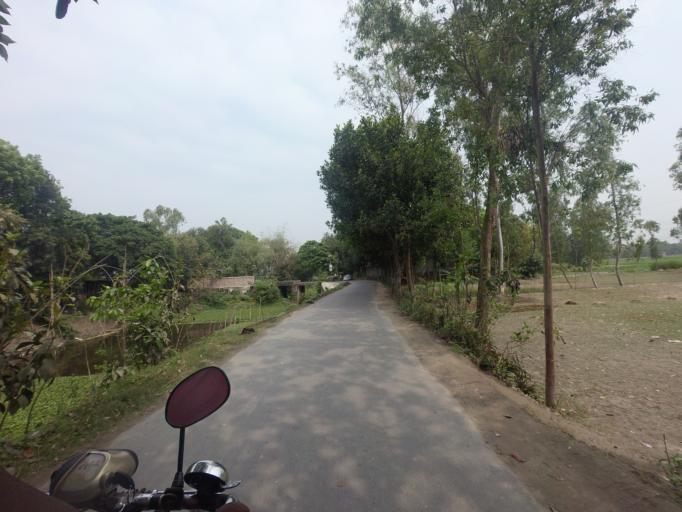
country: BD
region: Rajshahi
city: Sirajganj
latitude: 24.3505
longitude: 89.6762
